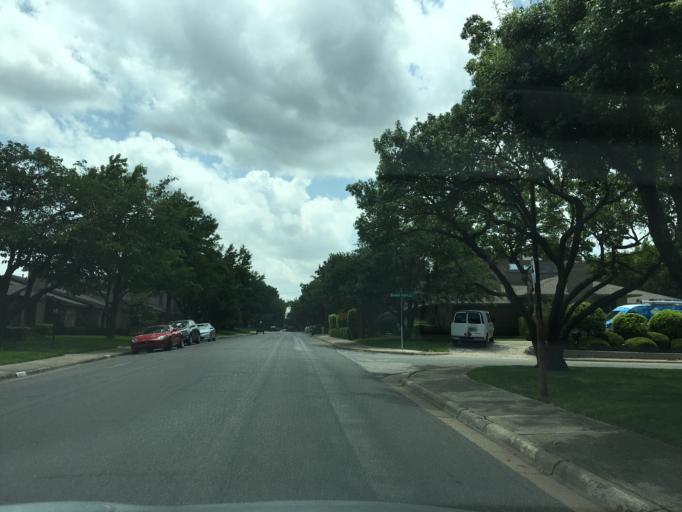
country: US
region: Texas
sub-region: Dallas County
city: University Park
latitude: 32.8941
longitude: -96.7772
